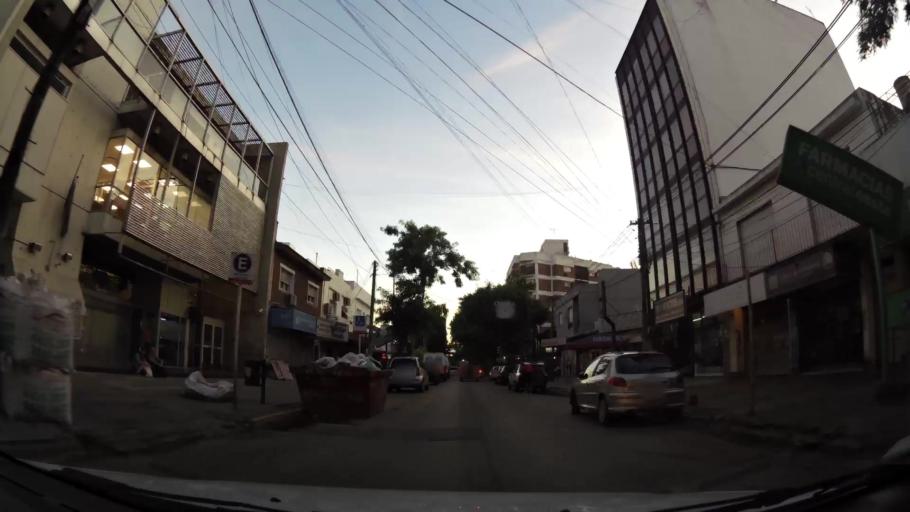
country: AR
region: Buenos Aires
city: Ituzaingo
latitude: -34.6533
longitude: -58.6428
